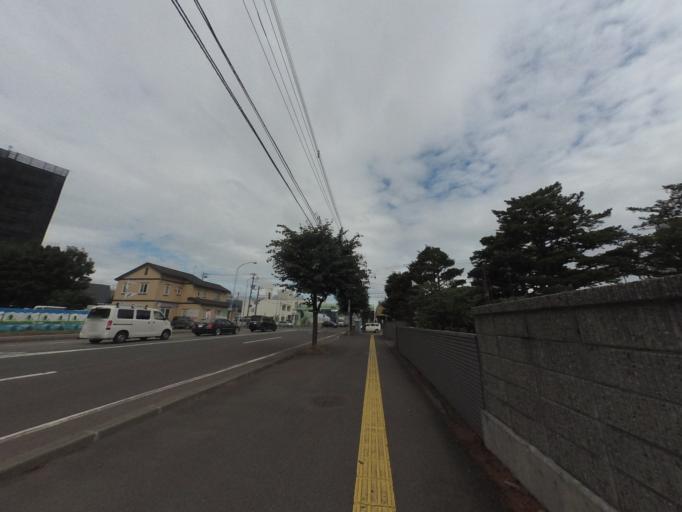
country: JP
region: Hokkaido
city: Sapporo
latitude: 43.0622
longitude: 141.3847
